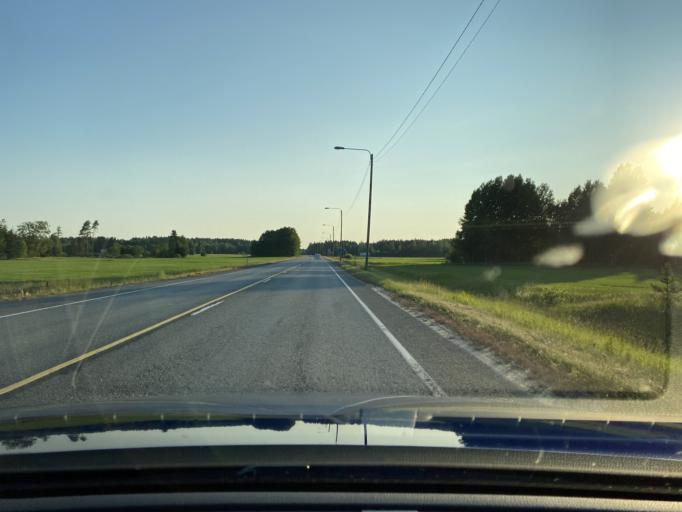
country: FI
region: Haeme
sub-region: Forssa
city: Tammela
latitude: 60.8290
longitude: 23.8350
